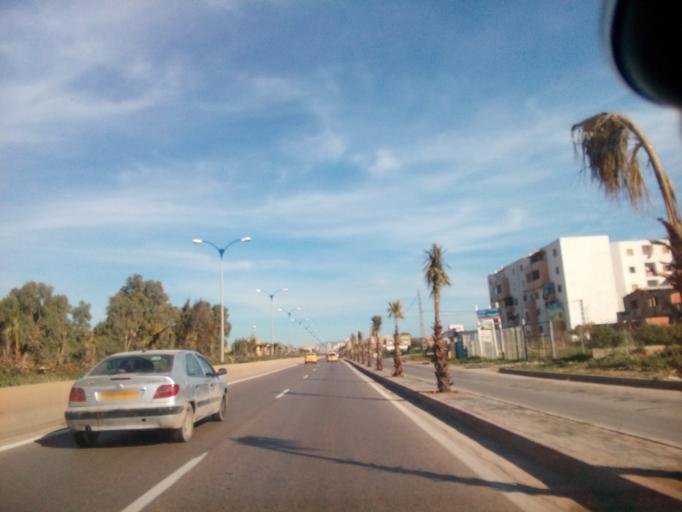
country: DZ
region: Mostaganem
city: Mostaganem
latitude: 35.9085
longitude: 0.0690
